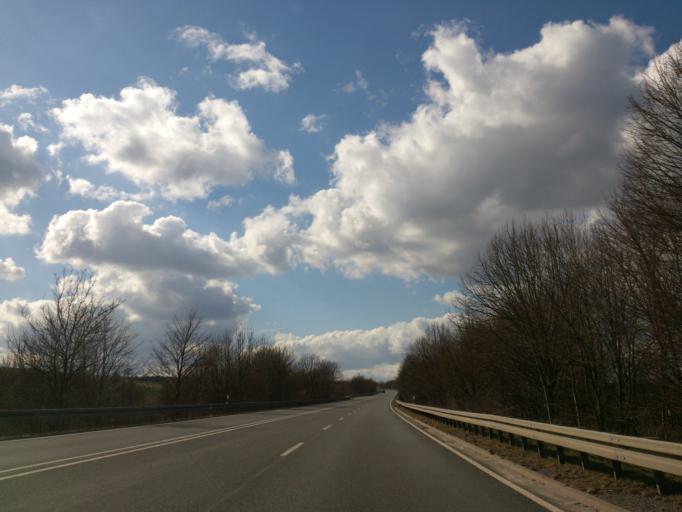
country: DE
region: North Rhine-Westphalia
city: Brakel
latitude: 51.7004
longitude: 9.2101
